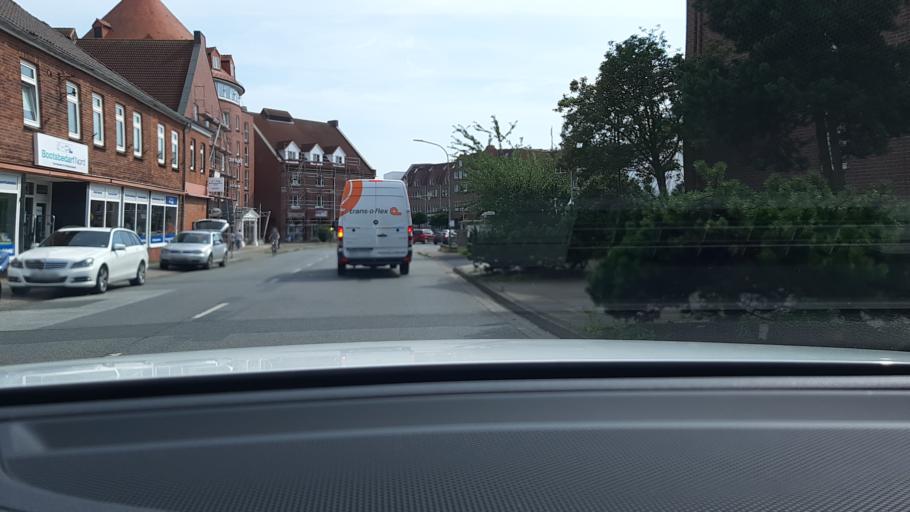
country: DE
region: Schleswig-Holstein
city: Stockelsdorf
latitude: 53.8871
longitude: 10.6514
